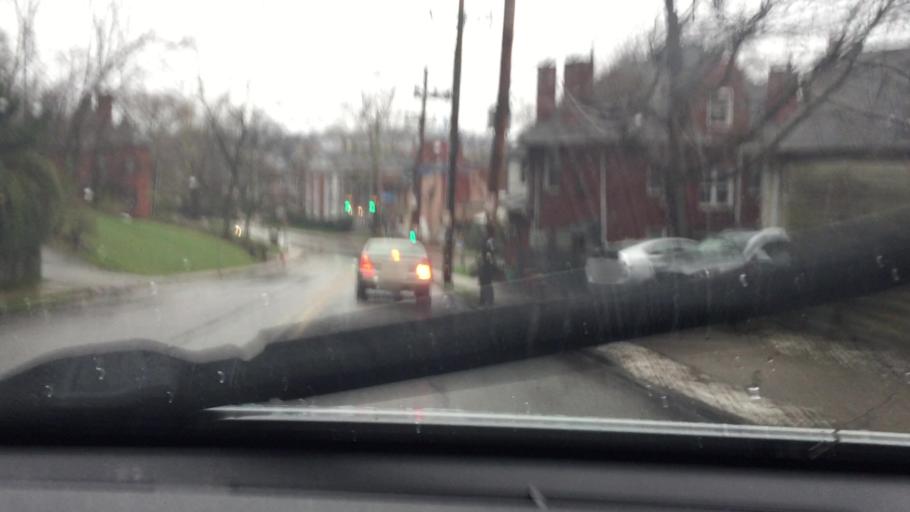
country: US
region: Pennsylvania
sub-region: Allegheny County
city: Bloomfield
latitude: 40.4475
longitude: -79.9361
